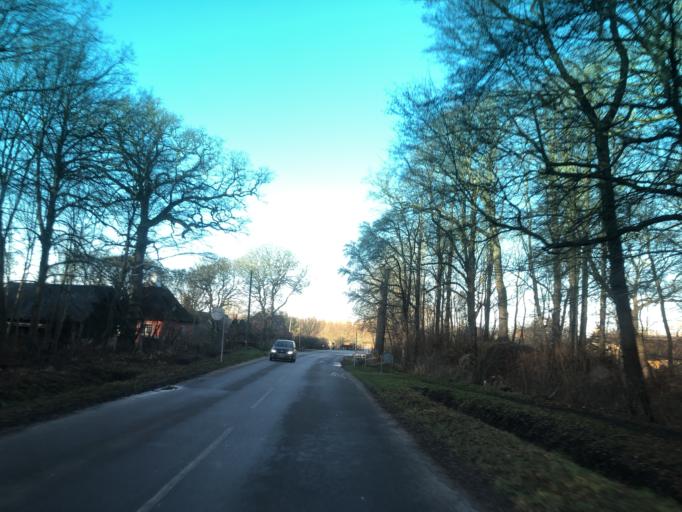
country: DK
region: Capital Region
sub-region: Tarnby Kommune
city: Tarnby
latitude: 55.5773
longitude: 12.5778
